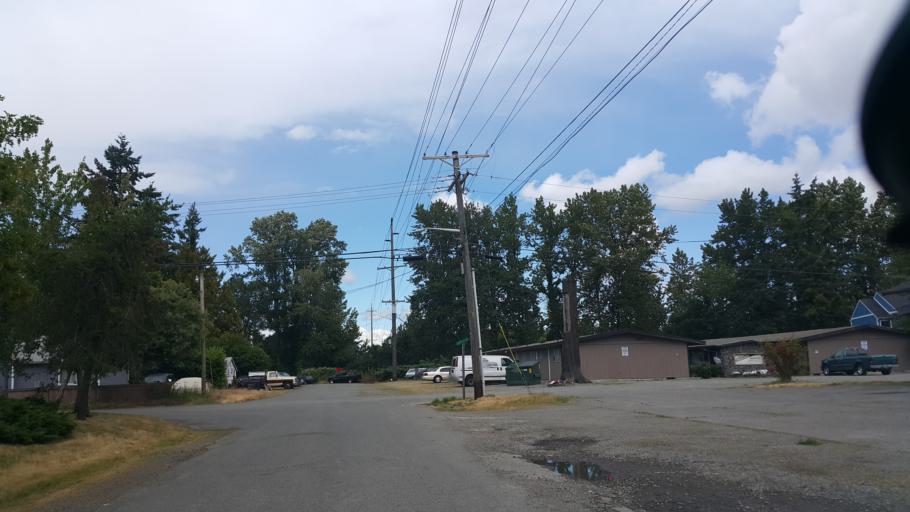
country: US
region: Washington
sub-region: Pierce County
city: McChord Air Force Base
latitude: 47.1419
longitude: -122.4993
